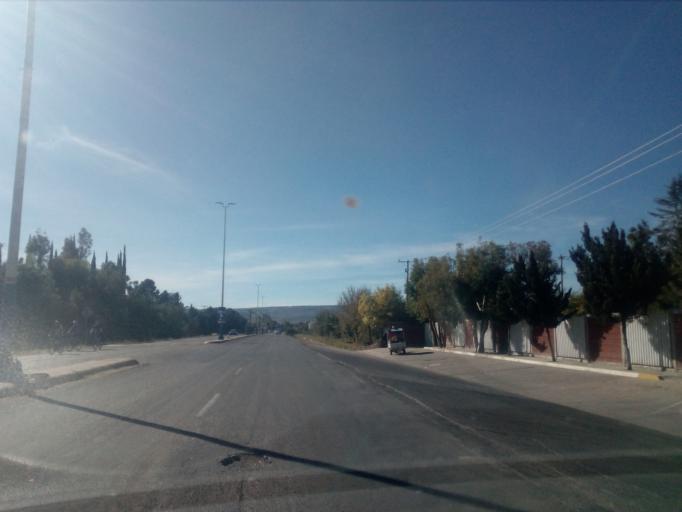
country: MX
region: Durango
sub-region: Durango
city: Sebastian Lerdo de Tejada
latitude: 23.9806
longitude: -104.6643
